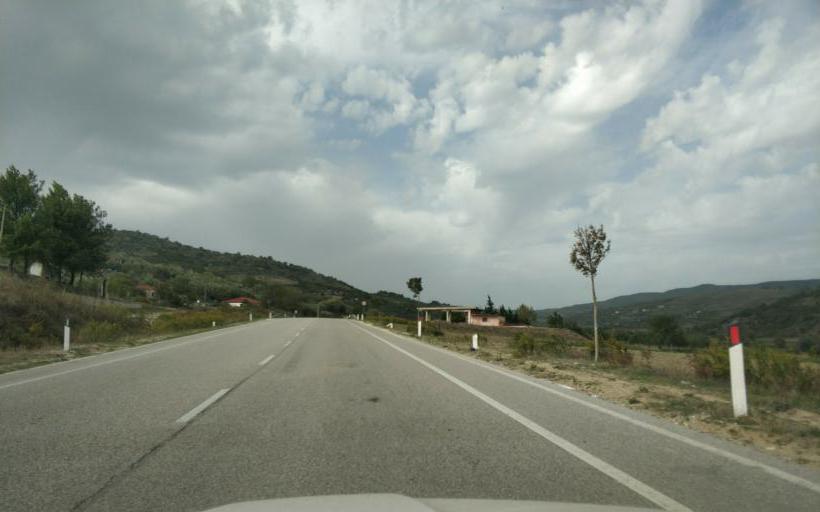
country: AL
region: Gjirokaster
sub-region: Rrethi i Tepelenes
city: Krahes
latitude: 40.4483
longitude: 19.8488
